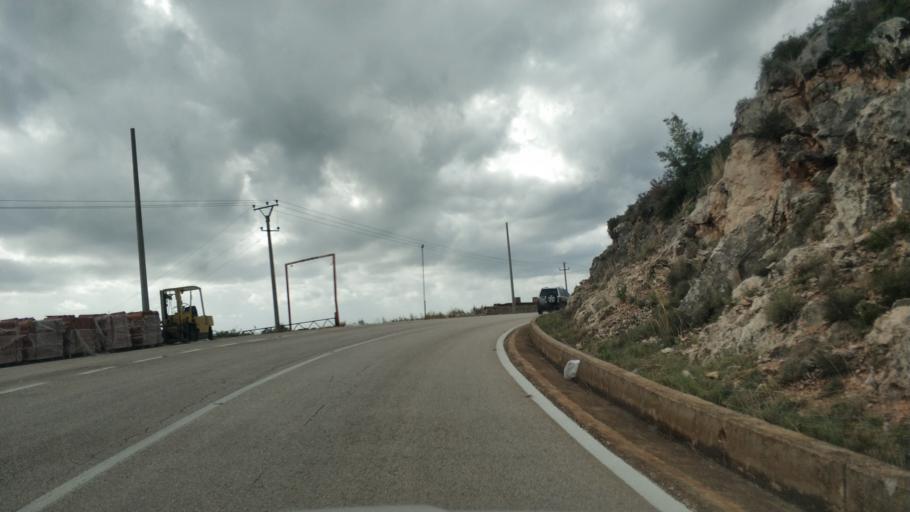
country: AL
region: Vlore
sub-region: Rrethi i Vlores
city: Vranisht
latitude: 40.1447
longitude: 19.6475
